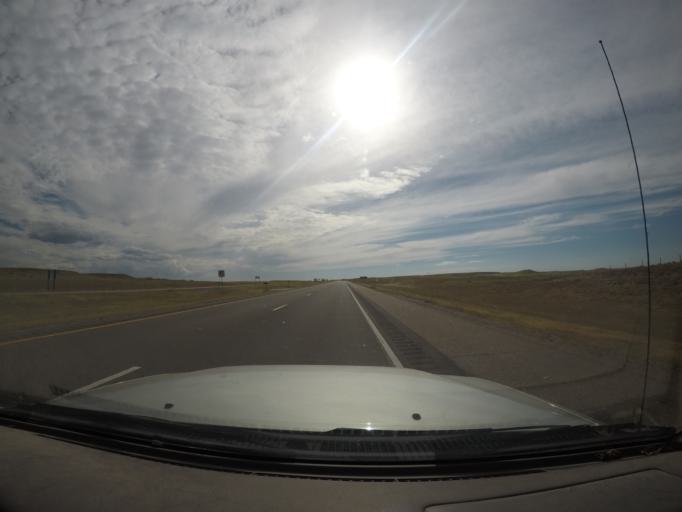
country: US
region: Nebraska
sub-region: Kimball County
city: Kimball
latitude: 41.2149
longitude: -103.6792
